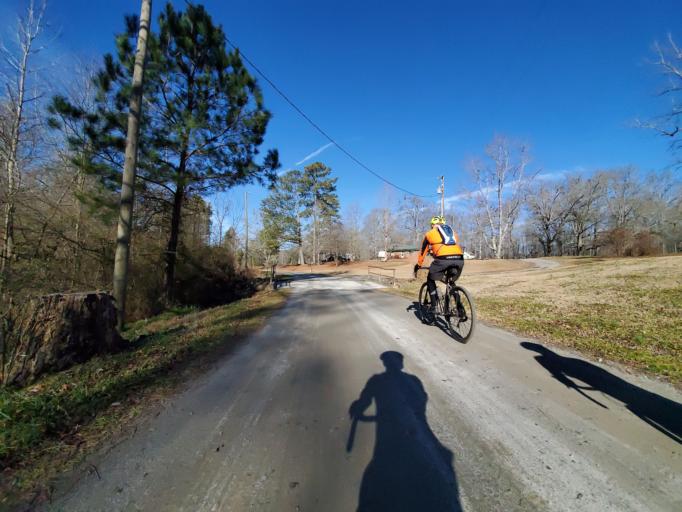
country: US
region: Georgia
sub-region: Fulton County
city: Chattahoochee Hills
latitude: 33.5518
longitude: -84.7969
